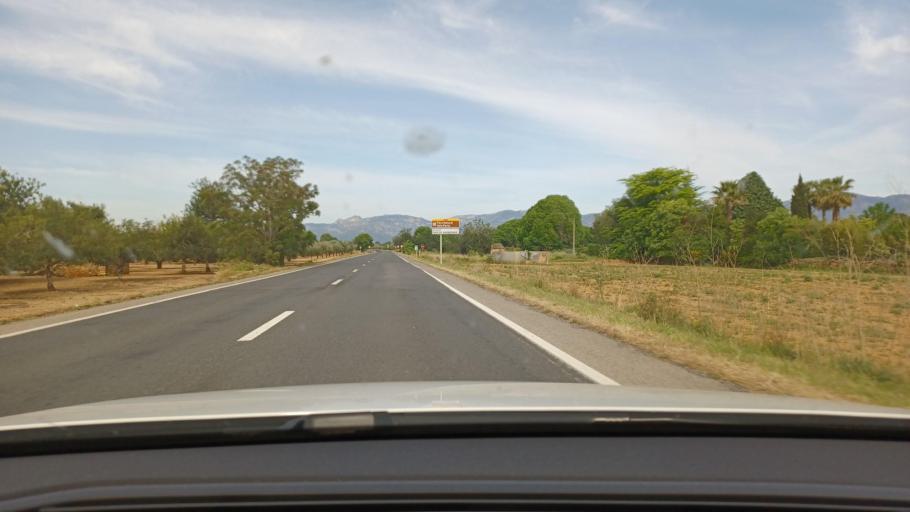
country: ES
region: Catalonia
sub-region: Provincia de Tarragona
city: Santa Barbara
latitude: 40.7058
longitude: 0.4895
